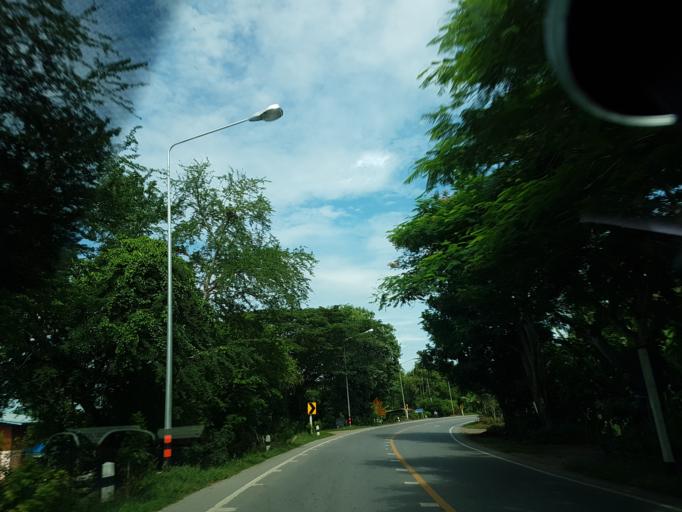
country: TH
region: Ang Thong
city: Chaiyo
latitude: 14.7212
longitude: 100.4963
